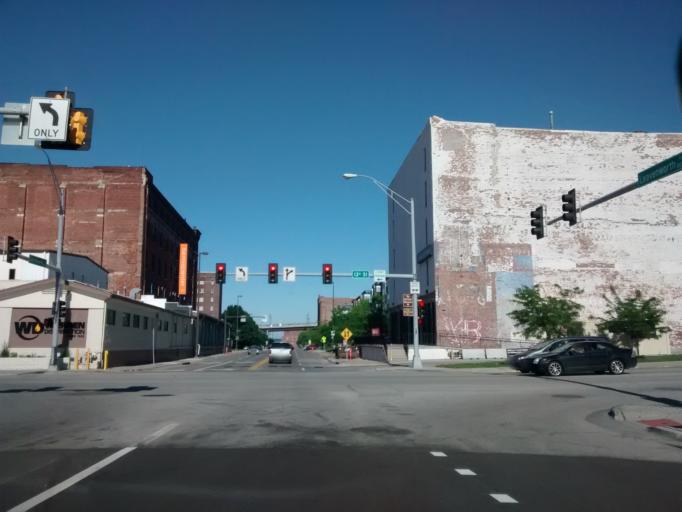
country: US
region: Nebraska
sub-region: Douglas County
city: Omaha
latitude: 41.2523
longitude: -95.9336
